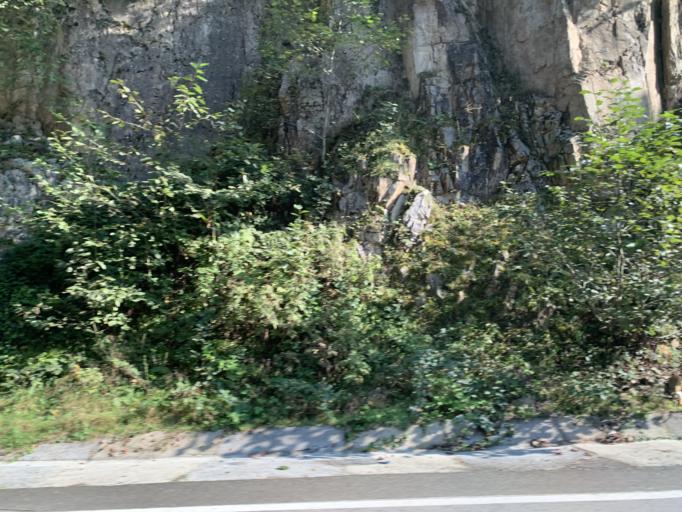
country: TR
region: Trabzon
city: Macka
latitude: 40.7047
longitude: 39.6504
